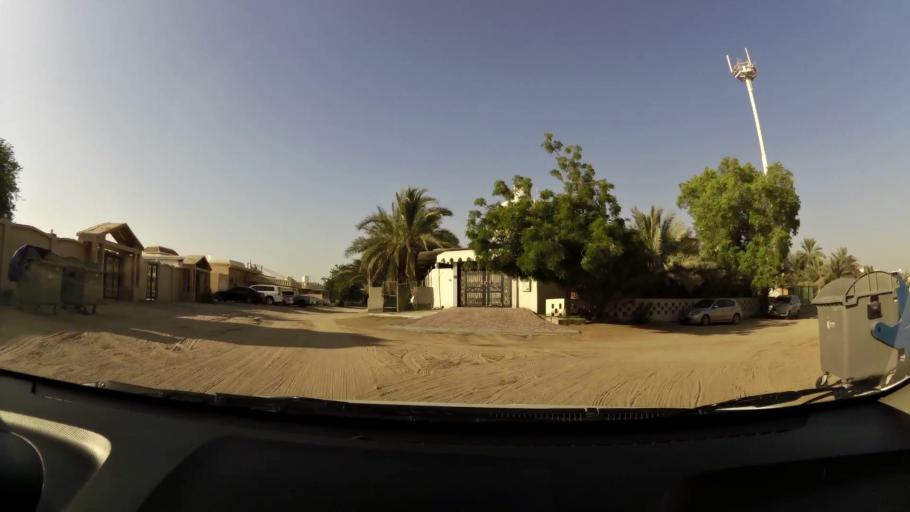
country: AE
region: Ajman
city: Ajman
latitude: 25.4028
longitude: 55.4677
